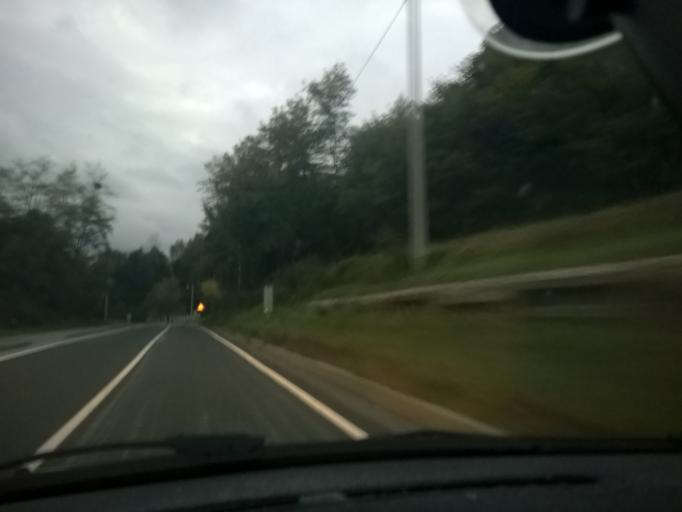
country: HR
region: Krapinsko-Zagorska
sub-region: Grad Krapina
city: Krapina
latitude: 46.1993
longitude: 15.8323
